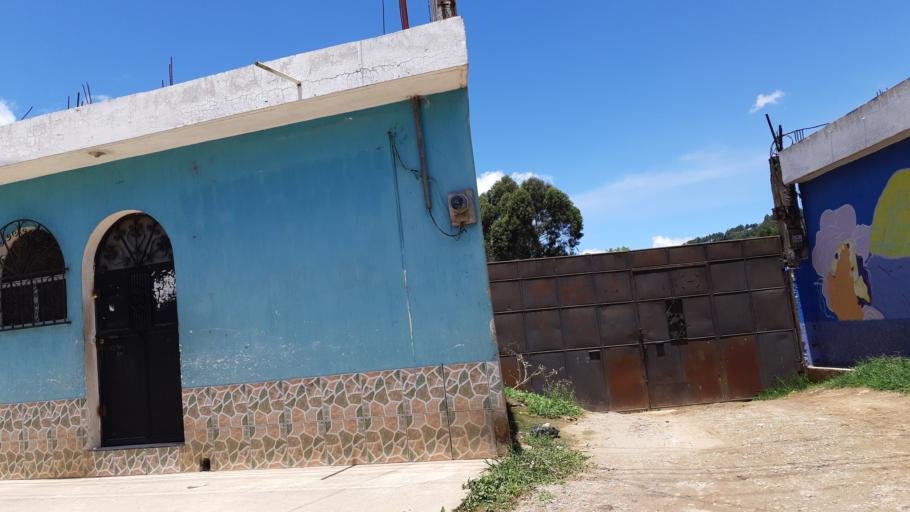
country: GT
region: Chimaltenango
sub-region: Municipio de Chimaltenango
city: Chimaltenango
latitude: 14.6639
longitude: -90.8449
